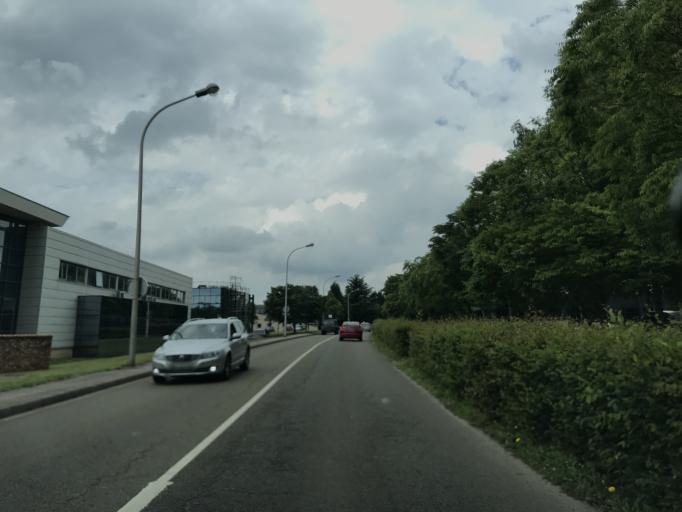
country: FR
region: Haute-Normandie
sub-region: Departement de la Seine-Maritime
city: Mont-Saint-Aignan
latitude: 49.4740
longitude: 1.0925
